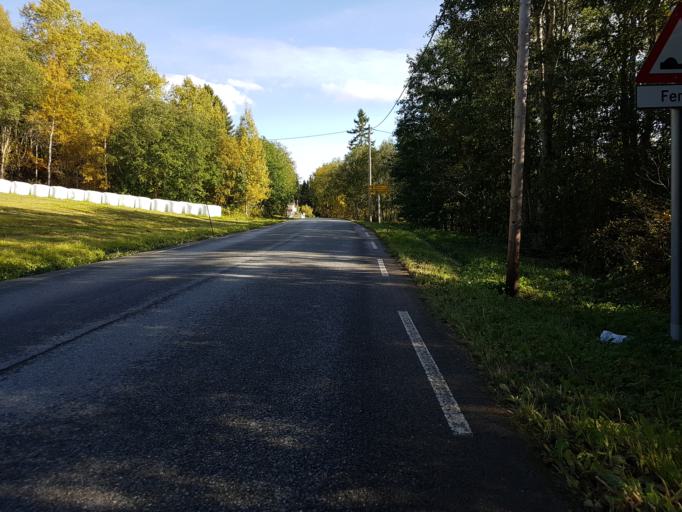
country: NO
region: Sor-Trondelag
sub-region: Malvik
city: Malvik
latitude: 63.3834
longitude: 10.5937
